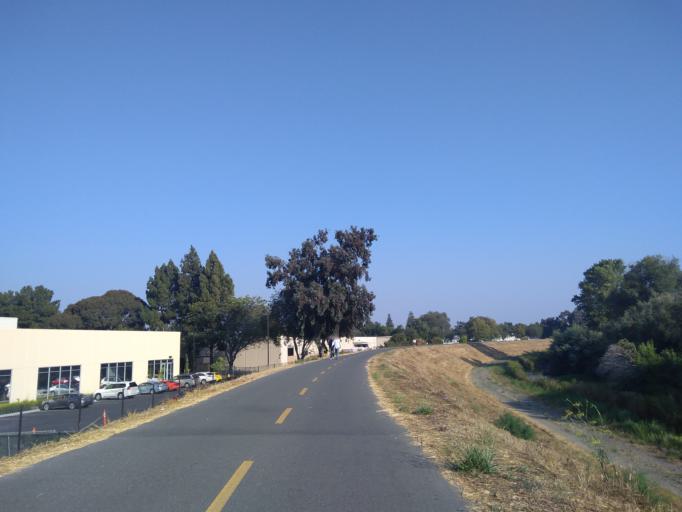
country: US
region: California
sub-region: Santa Clara County
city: Santa Clara
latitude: 37.3884
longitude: -121.9364
